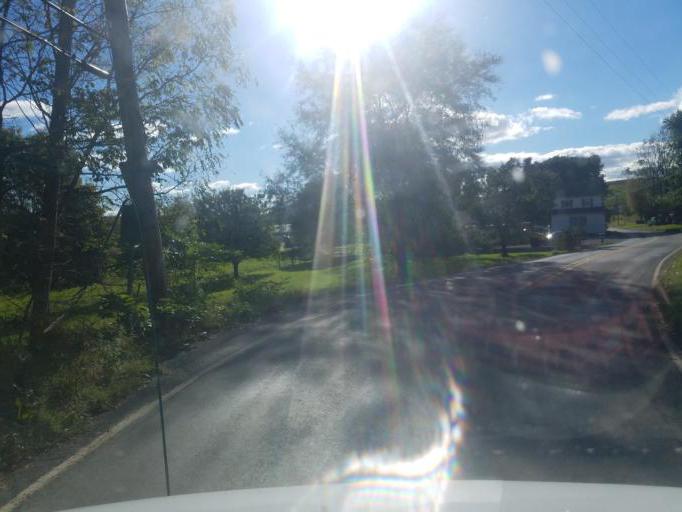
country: US
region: Pennsylvania
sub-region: Franklin County
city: Guilford Siding
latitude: 39.8113
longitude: -77.6213
